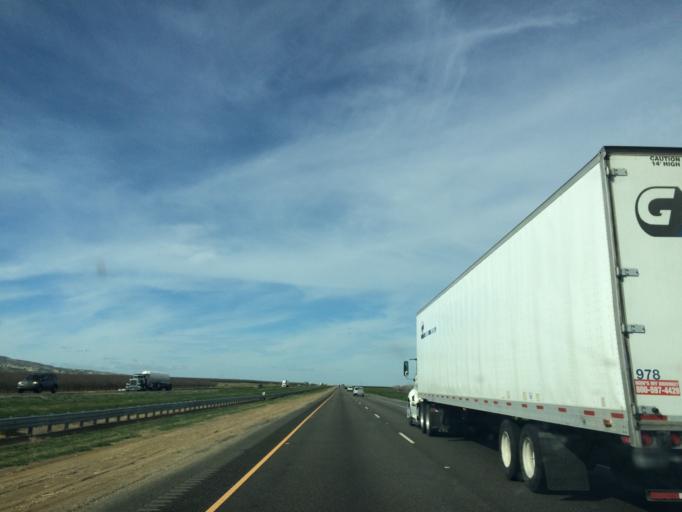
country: US
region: California
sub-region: Fresno County
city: Firebaugh
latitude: 36.6945
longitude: -120.6647
